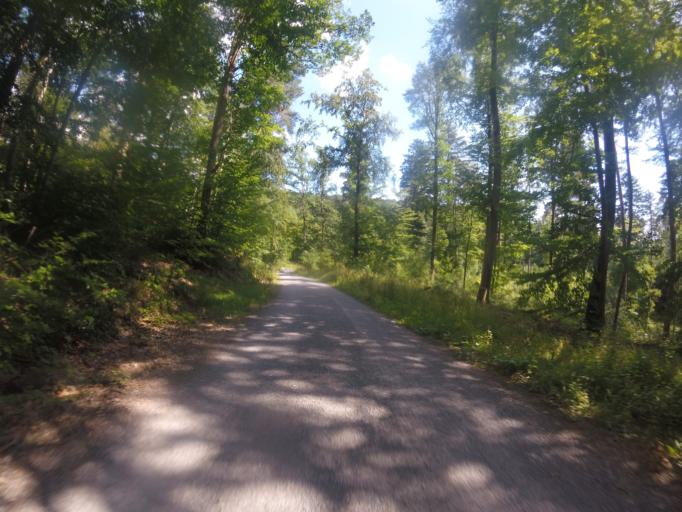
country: DE
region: Baden-Wuerttemberg
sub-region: Regierungsbezirk Stuttgart
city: Beilstein
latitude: 49.0681
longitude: 9.3349
